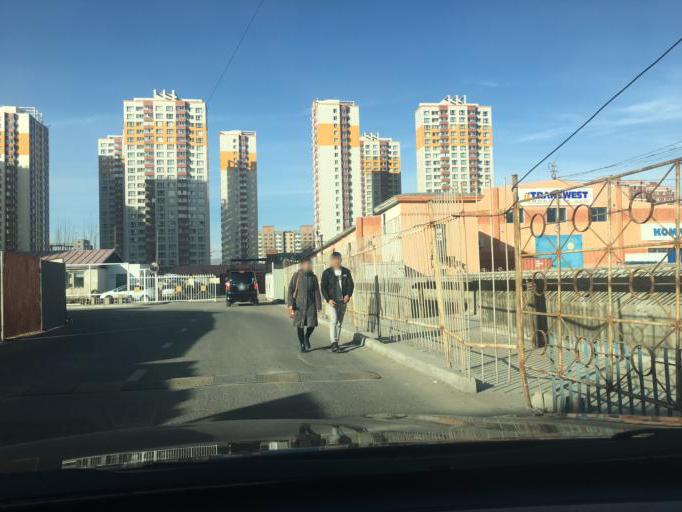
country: MN
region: Ulaanbaatar
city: Ulaanbaatar
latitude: 47.9037
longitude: 106.8980
